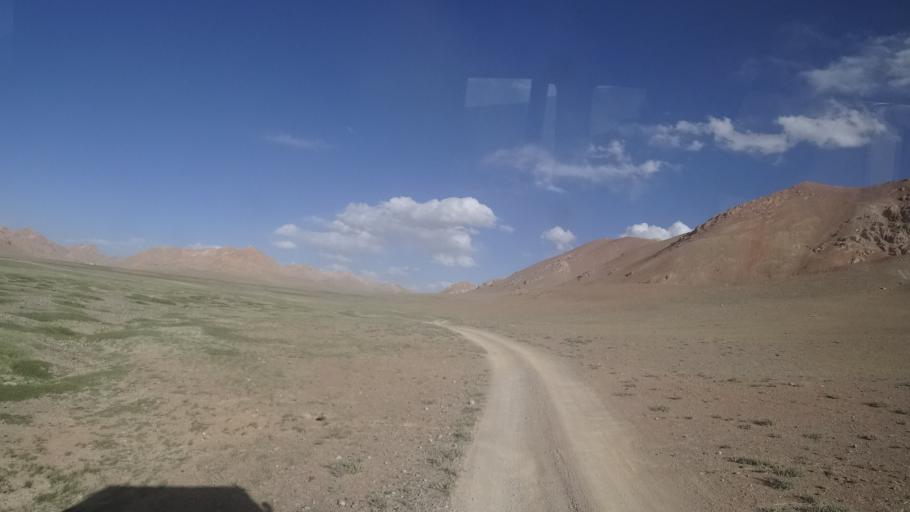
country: TJ
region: Gorno-Badakhshan
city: Murghob
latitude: 37.6566
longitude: 74.1659
